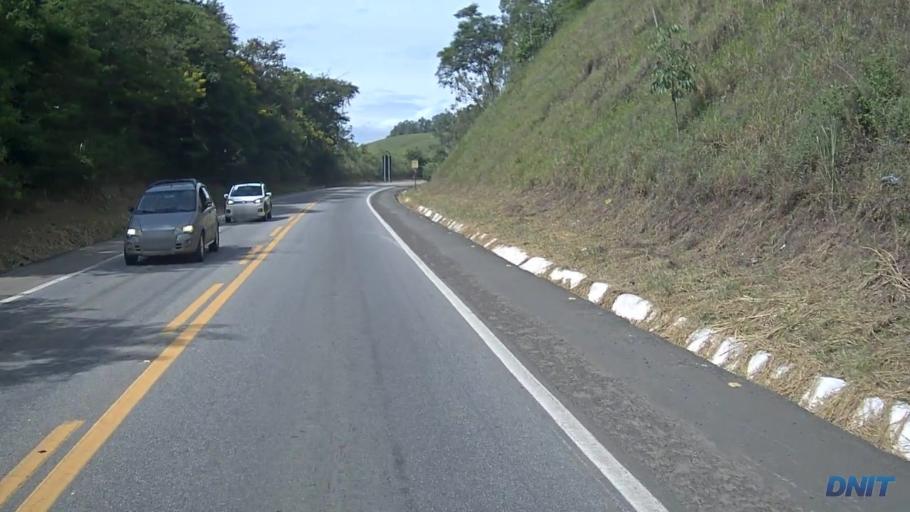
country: BR
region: Minas Gerais
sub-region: Ipatinga
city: Ipatinga
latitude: -19.4266
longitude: -42.5007
